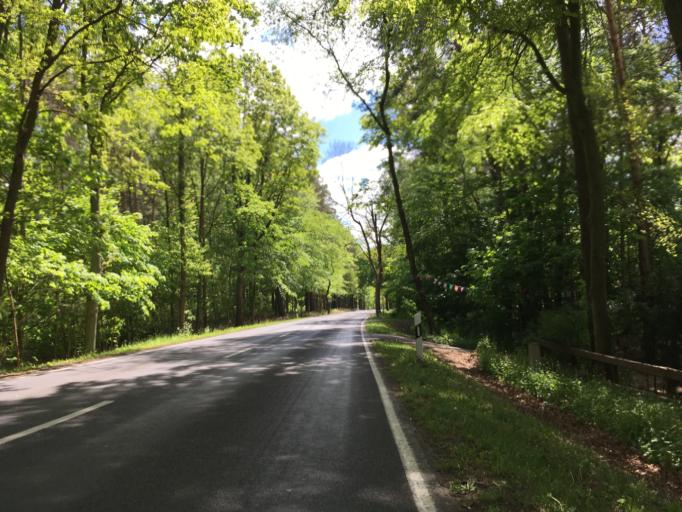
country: DE
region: Brandenburg
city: Marienwerder
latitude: 52.7823
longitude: 13.5571
